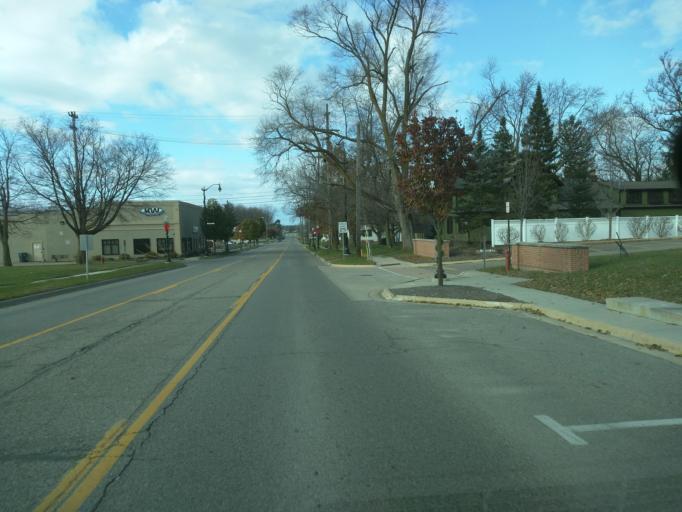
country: US
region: Michigan
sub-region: Livingston County
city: Fowlerville
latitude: 42.6607
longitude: -84.0749
